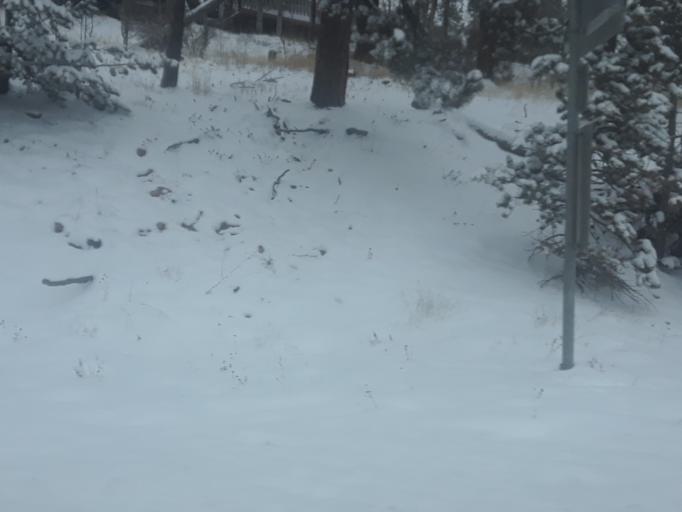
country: US
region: Colorado
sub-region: Boulder County
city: Coal Creek
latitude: 39.9244
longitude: -105.3987
